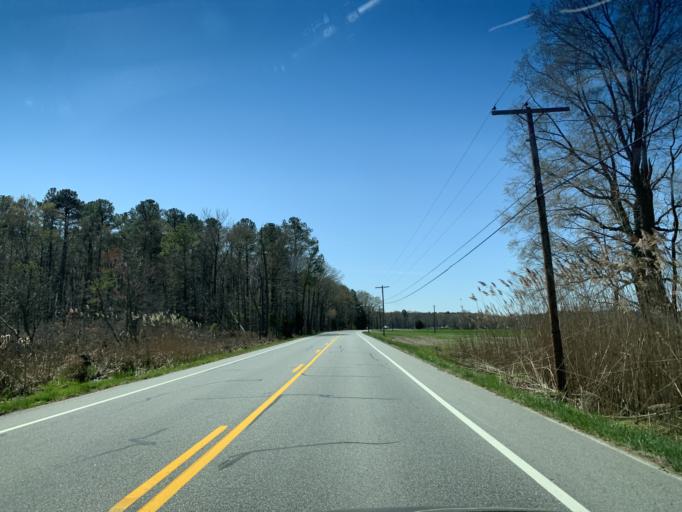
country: US
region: Maryland
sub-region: Talbot County
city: Easton
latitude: 38.8192
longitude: -76.0441
